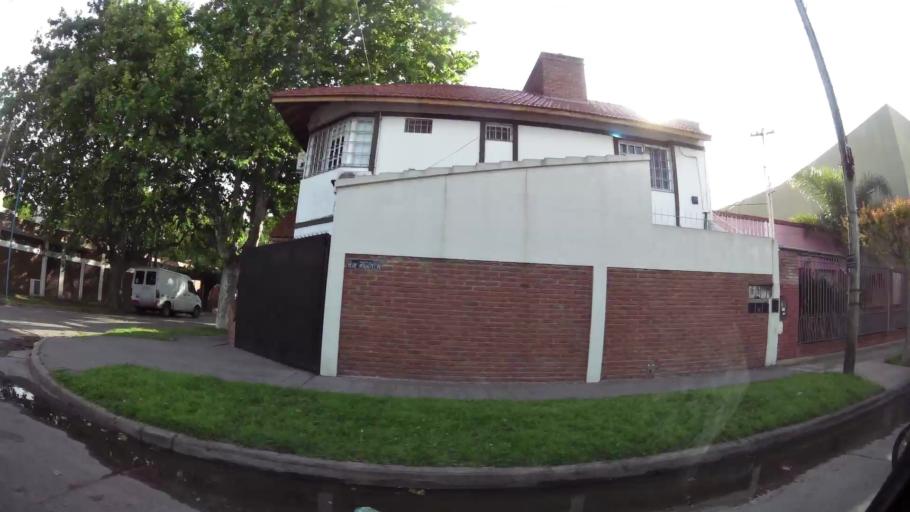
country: AR
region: Buenos Aires
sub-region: Partido de Quilmes
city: Quilmes
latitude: -34.7378
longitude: -58.2564
